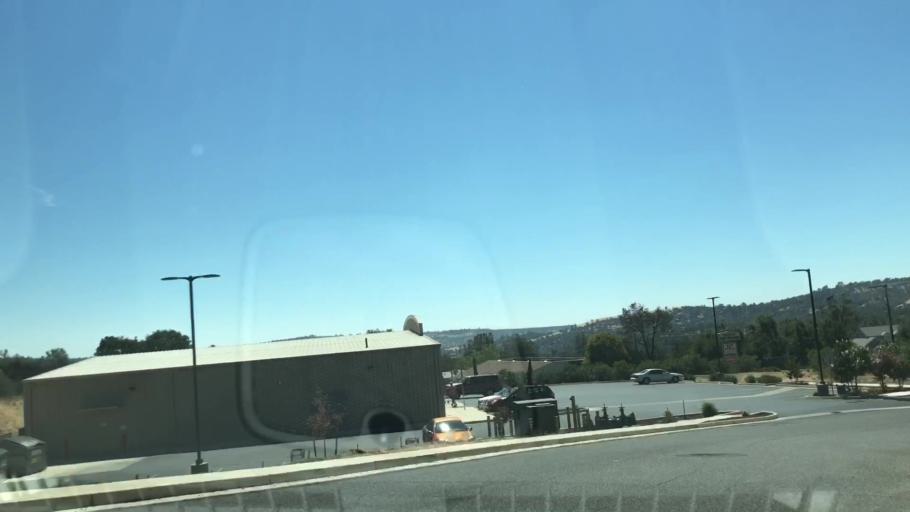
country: US
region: California
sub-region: Calaveras County
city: Copperopolis
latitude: 37.9373
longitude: -120.6041
